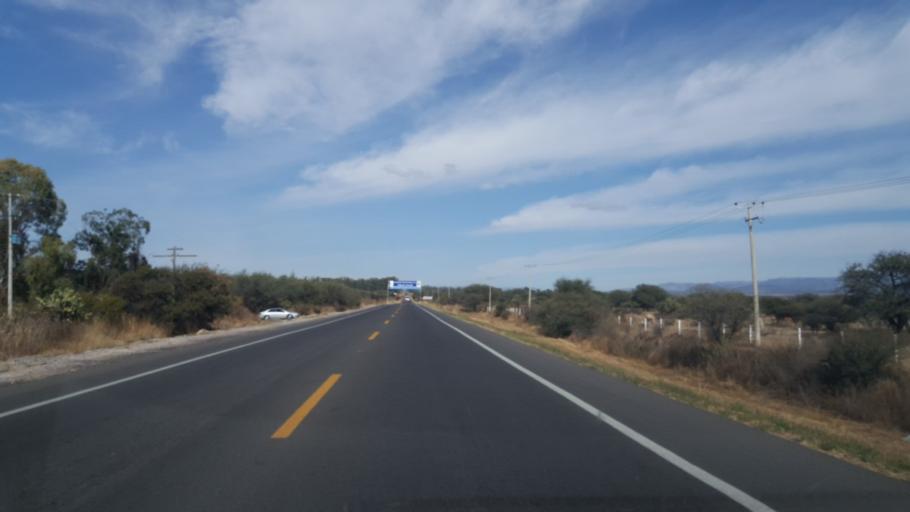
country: MX
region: Jalisco
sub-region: Lagos de Moreno
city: Cristeros [Fraccionamiento]
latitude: 21.2685
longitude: -101.9431
